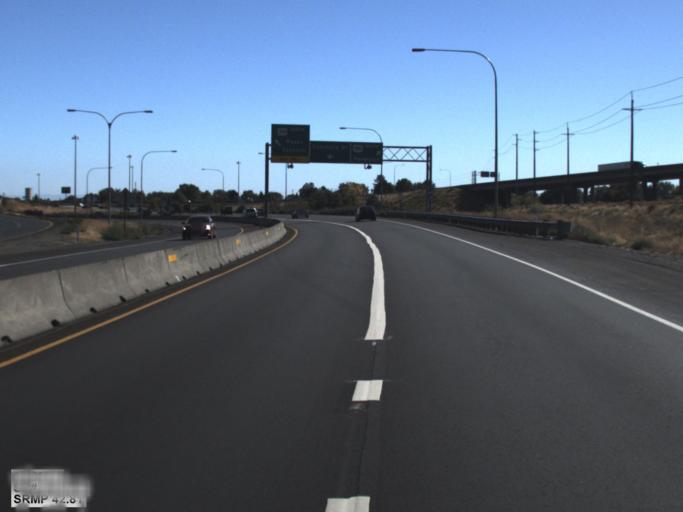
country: US
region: Washington
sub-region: Benton County
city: Kennewick
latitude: 46.2176
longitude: -119.1457
